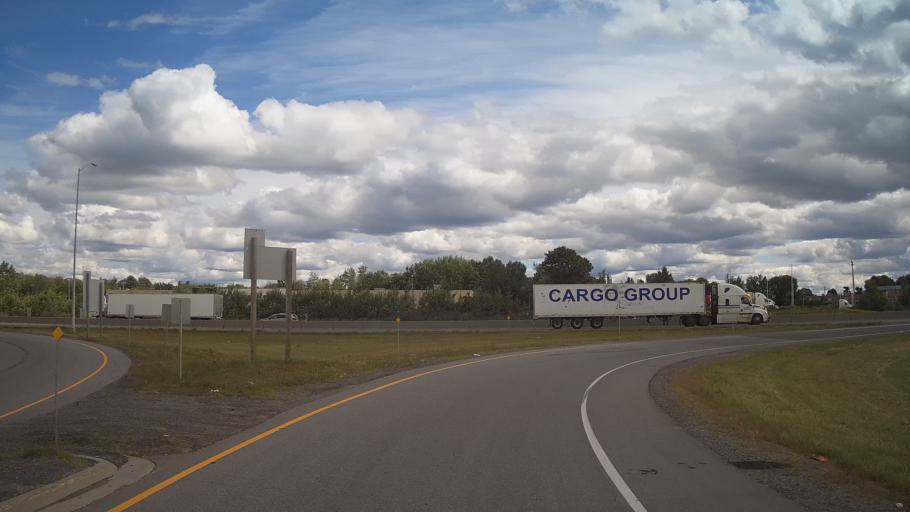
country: CA
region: Ontario
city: Prescott
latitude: 44.7247
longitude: -75.5242
